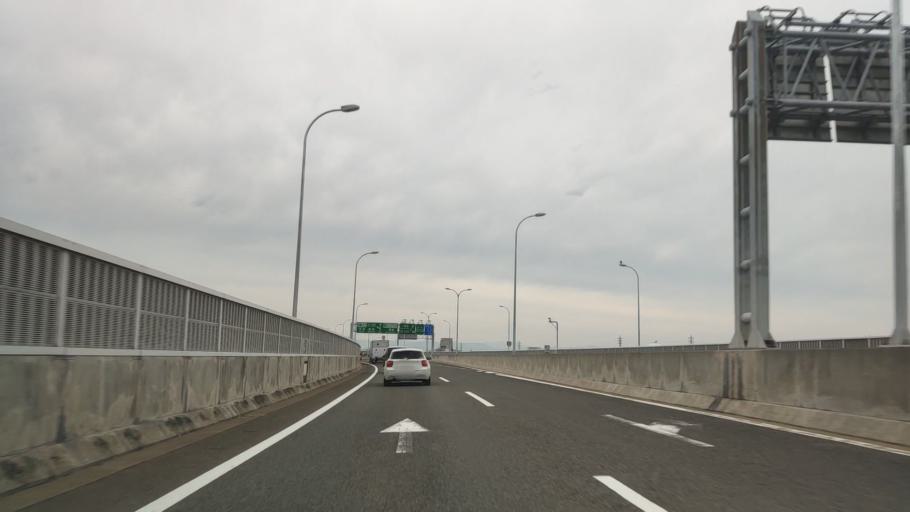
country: JP
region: Aichi
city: Iwakura
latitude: 35.2638
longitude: 136.8399
